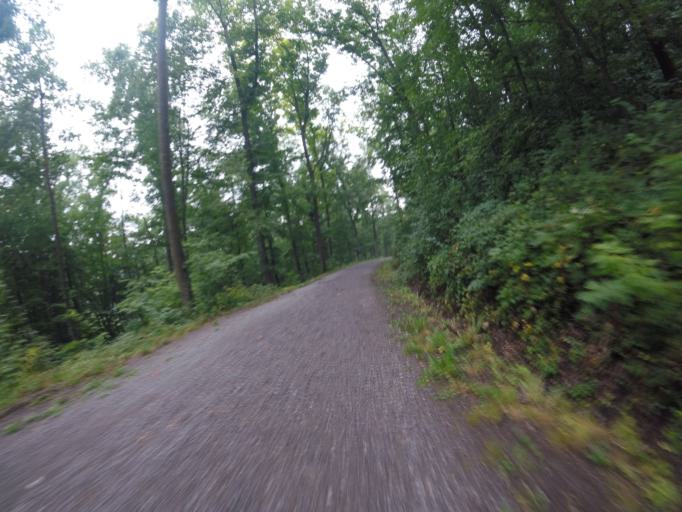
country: DE
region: Baden-Wuerttemberg
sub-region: Regierungsbezirk Stuttgart
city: Oppenweiler
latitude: 48.9830
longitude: 9.4340
